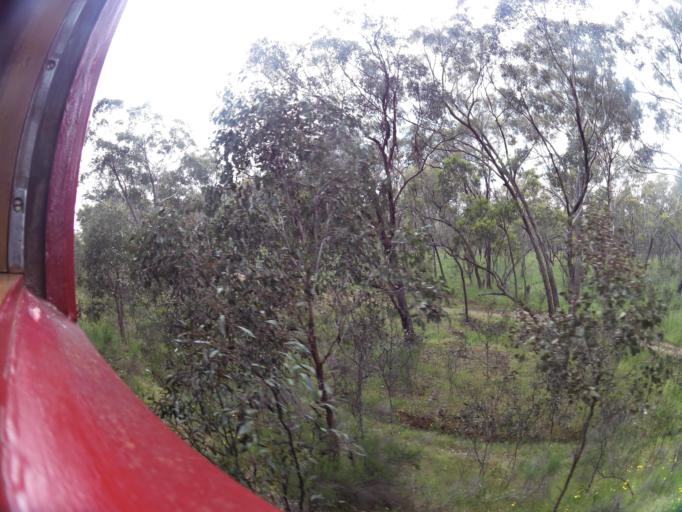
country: AU
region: Victoria
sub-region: Mount Alexander
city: Castlemaine
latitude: -37.0040
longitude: 144.1124
